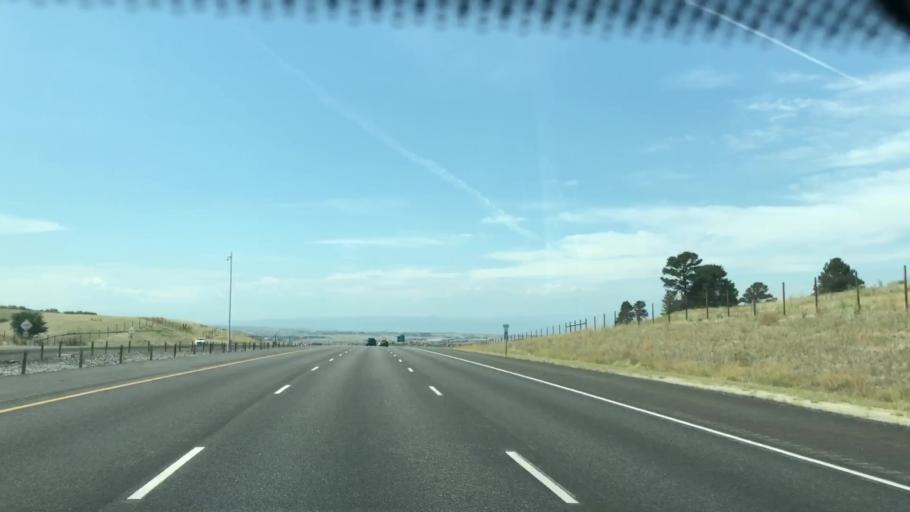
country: US
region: Colorado
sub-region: Douglas County
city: Parker
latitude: 39.5694
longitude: -104.7563
